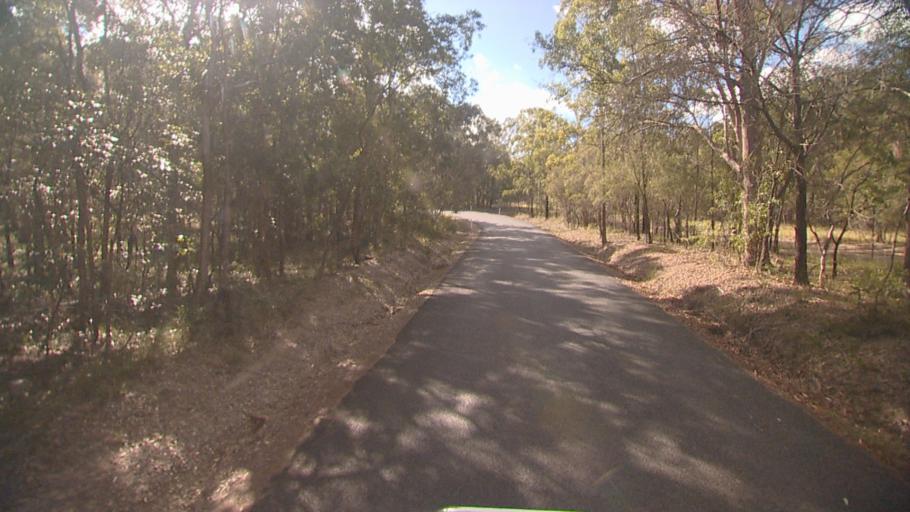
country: AU
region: Queensland
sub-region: Logan
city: Beenleigh
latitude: -27.6528
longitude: 153.2301
